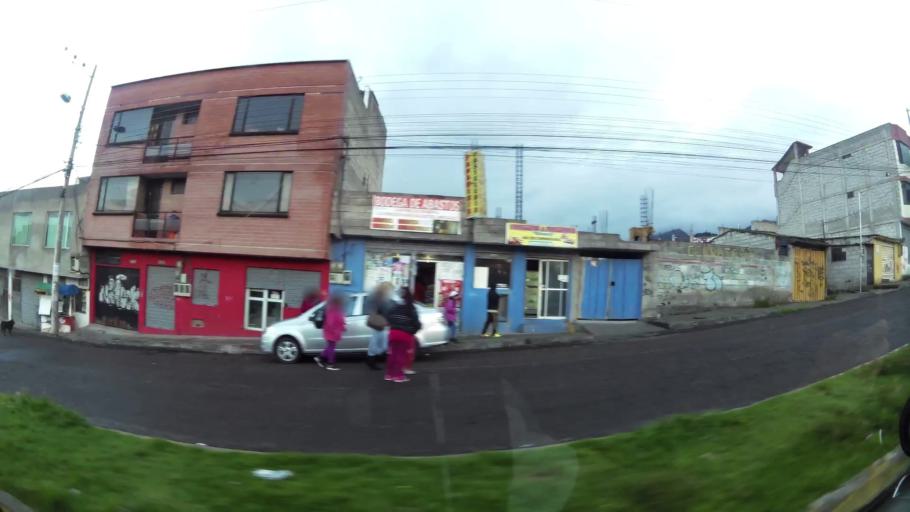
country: EC
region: Pichincha
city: Quito
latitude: -0.0908
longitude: -78.5211
